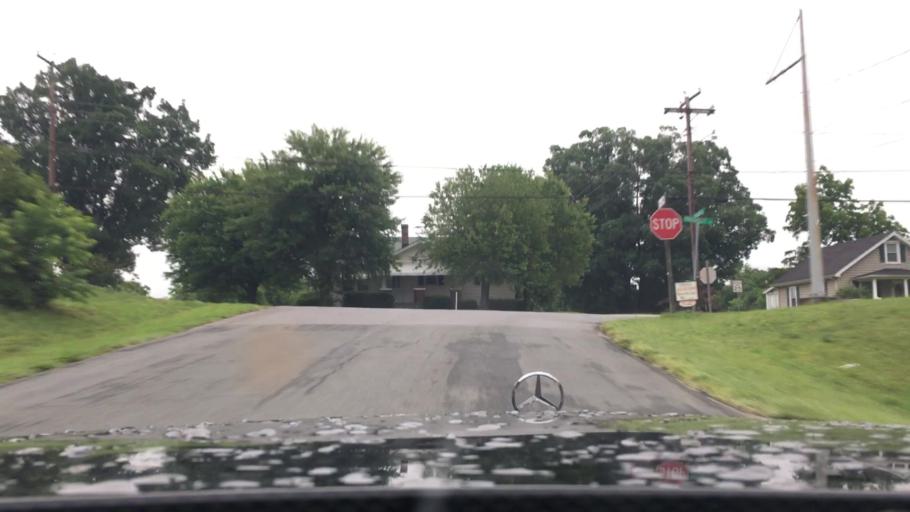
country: US
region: Virginia
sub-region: Pittsylvania County
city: Hurt
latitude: 37.0954
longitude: -79.2950
